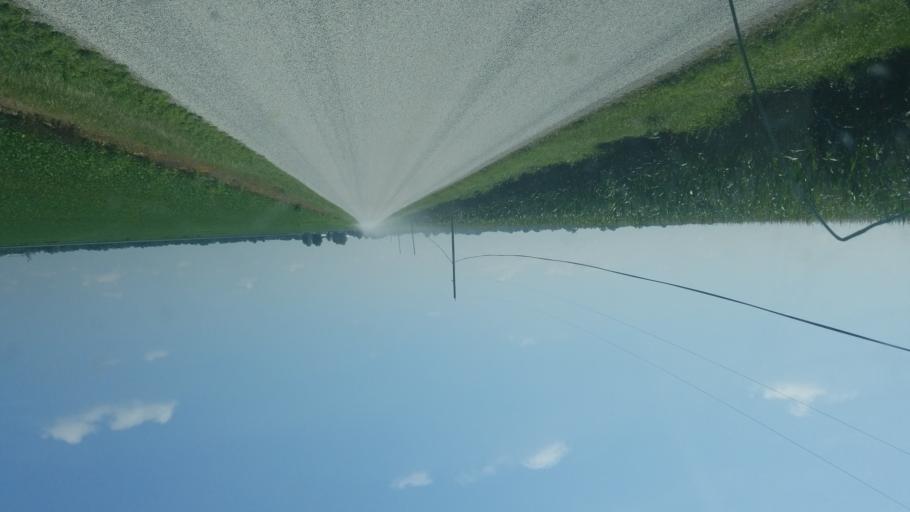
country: US
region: Ohio
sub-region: Hardin County
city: Ada
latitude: 40.6998
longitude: -83.7304
